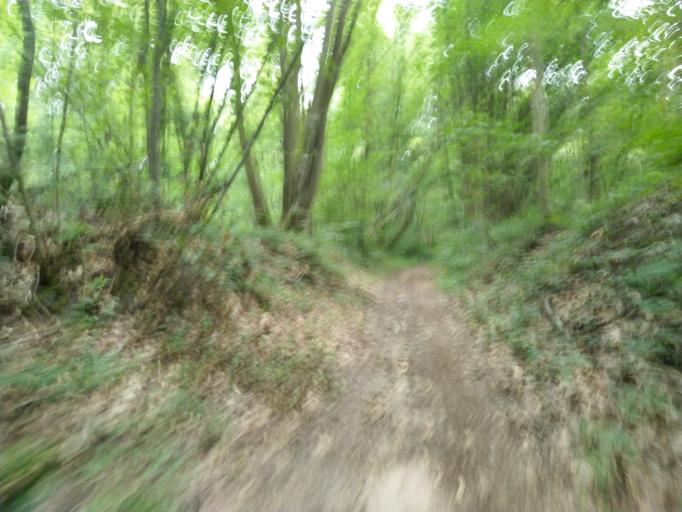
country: BE
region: Wallonia
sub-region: Province du Hainaut
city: Mons
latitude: 50.4941
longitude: 3.9489
